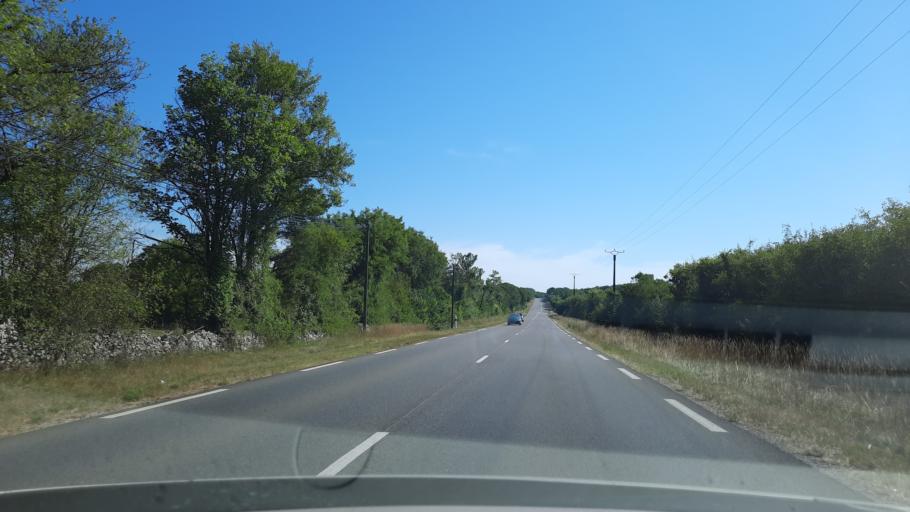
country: FR
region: Midi-Pyrenees
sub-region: Departement du Tarn-et-Garonne
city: Caylus
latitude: 44.2201
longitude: 1.7394
